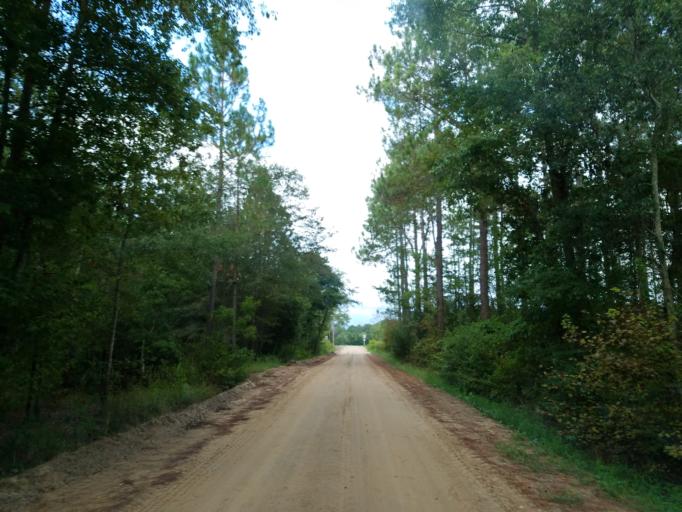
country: US
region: Georgia
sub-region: Cook County
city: Sparks
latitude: 31.2357
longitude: -83.4567
